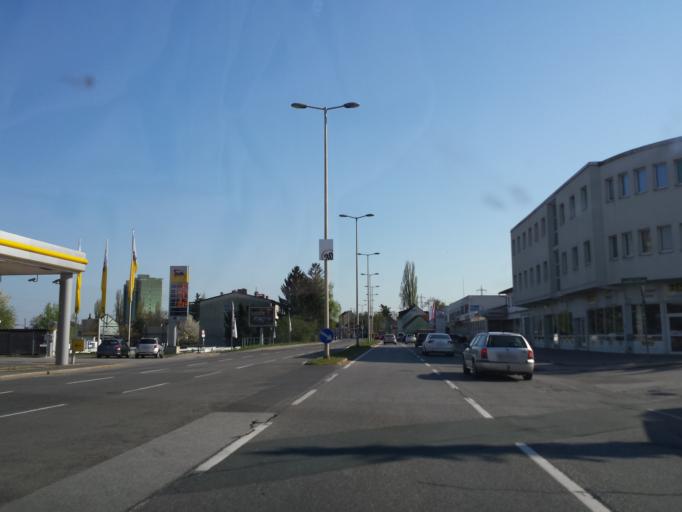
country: AT
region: Styria
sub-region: Graz Stadt
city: Goesting
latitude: 47.0985
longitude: 15.4037
